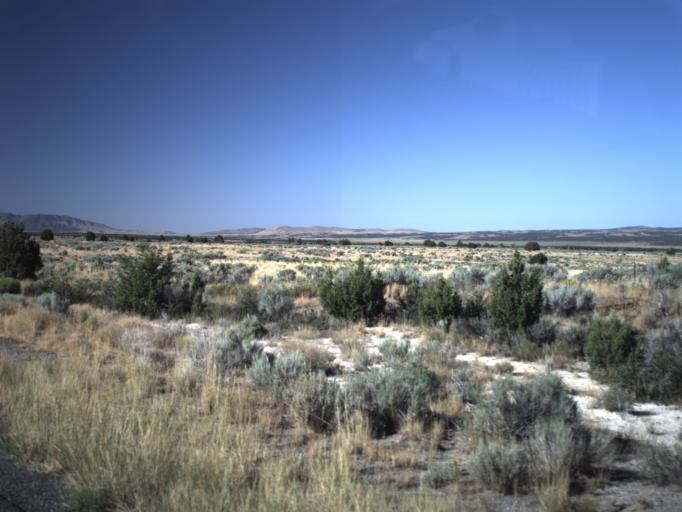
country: US
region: Utah
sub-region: Juab County
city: Mona
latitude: 39.8747
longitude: -112.1381
